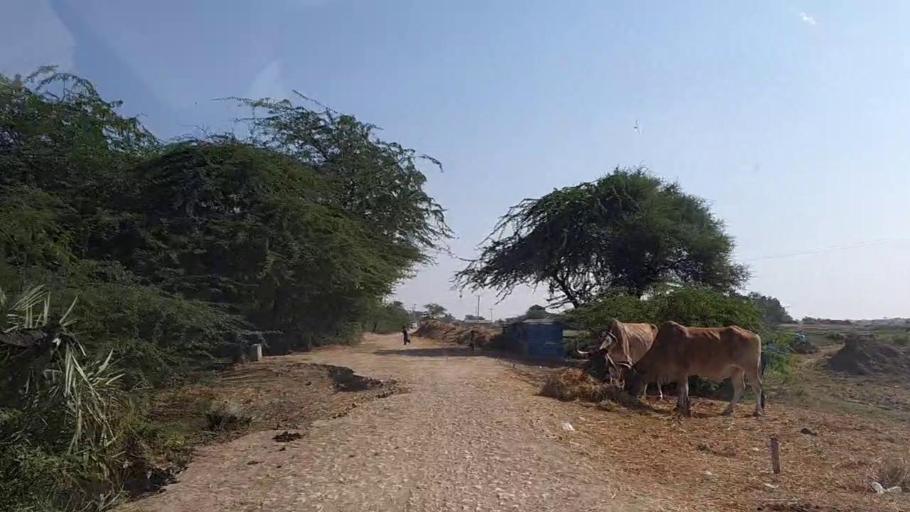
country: PK
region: Sindh
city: Thatta
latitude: 24.7648
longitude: 67.9443
